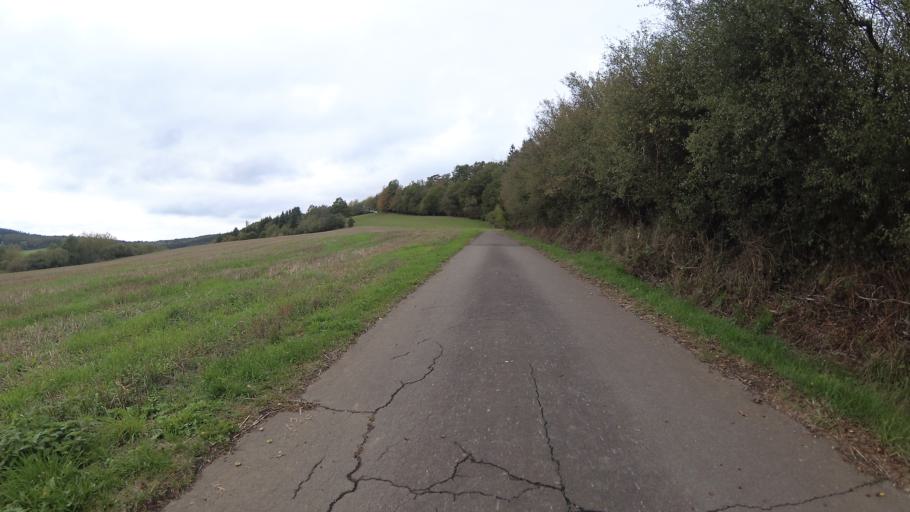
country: DE
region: Rheinland-Pfalz
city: Breitenbach
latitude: 49.4565
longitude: 7.2301
